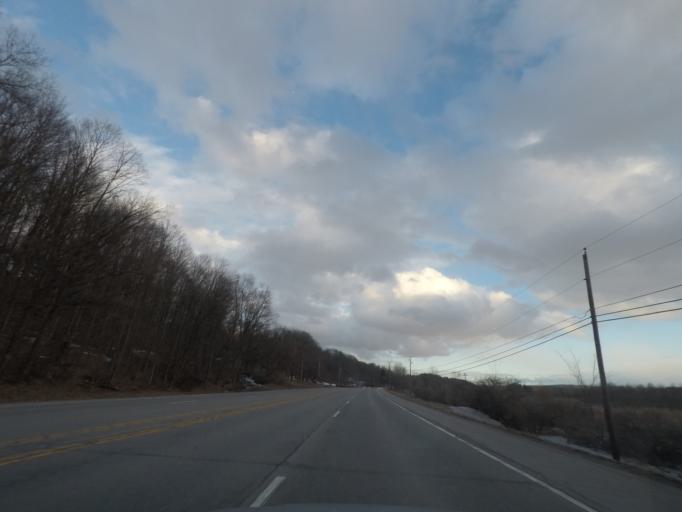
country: US
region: New York
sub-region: Herkimer County
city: Little Falls
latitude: 43.0315
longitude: -74.8001
